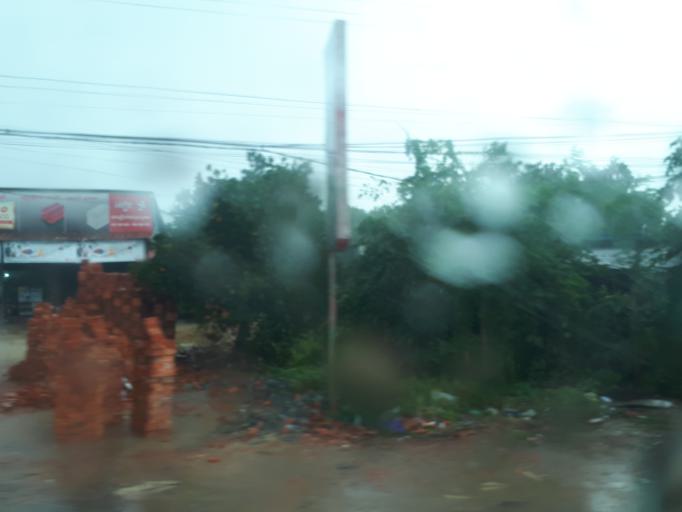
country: KH
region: Kandal
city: Ta Khmau
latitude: 11.5247
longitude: 105.0171
